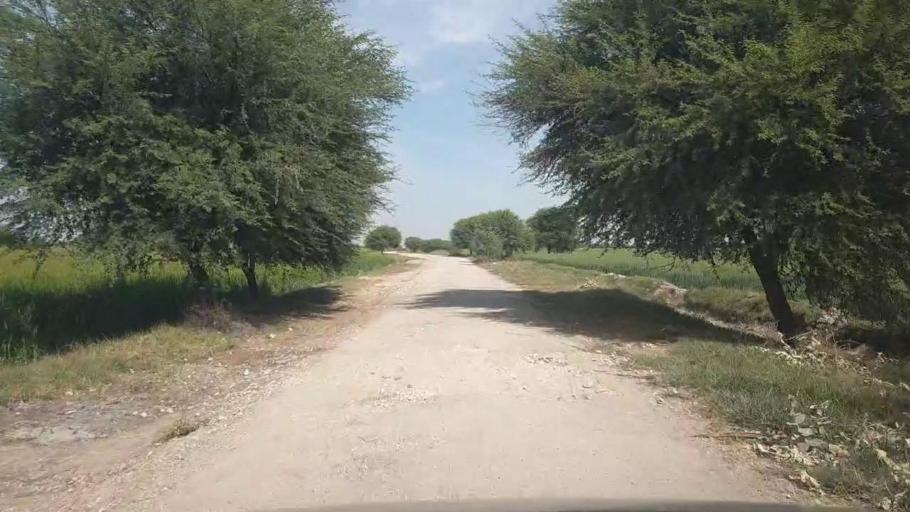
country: PK
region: Sindh
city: Kunri
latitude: 25.2178
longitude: 69.6446
